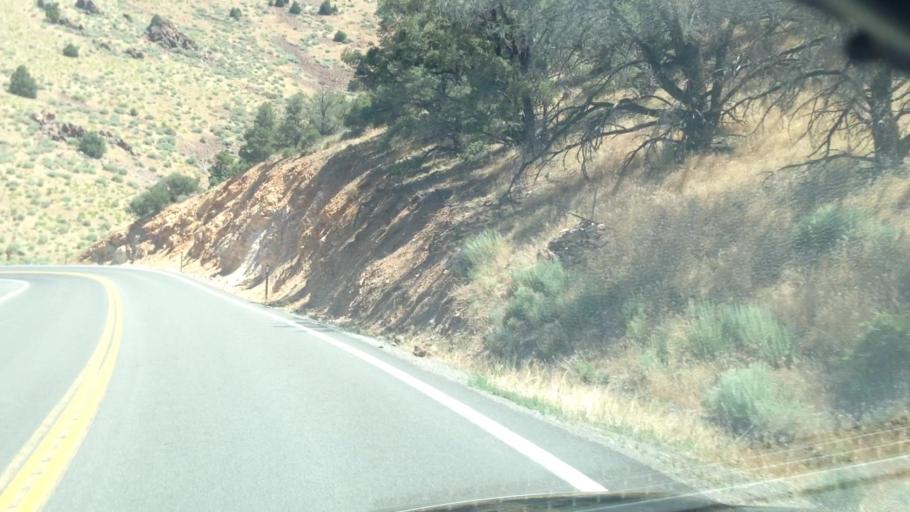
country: US
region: Nevada
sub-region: Storey County
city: Virginia City
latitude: 39.3765
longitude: -119.6931
